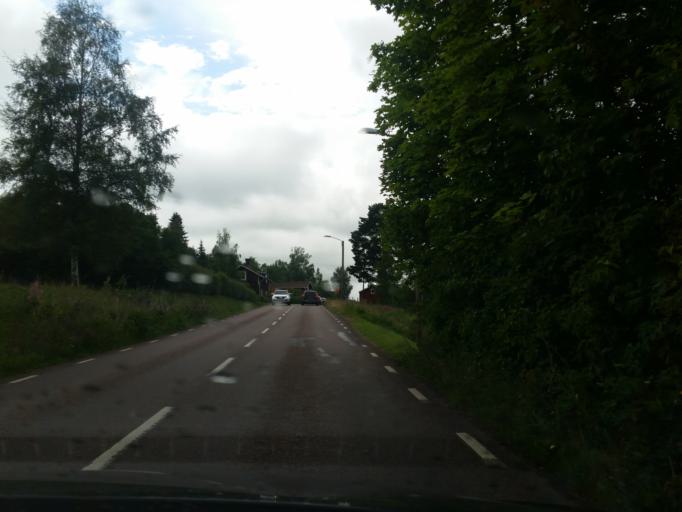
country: SE
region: Dalarna
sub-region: Leksand Municipality
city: Leksand
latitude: 60.7161
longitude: 14.9710
